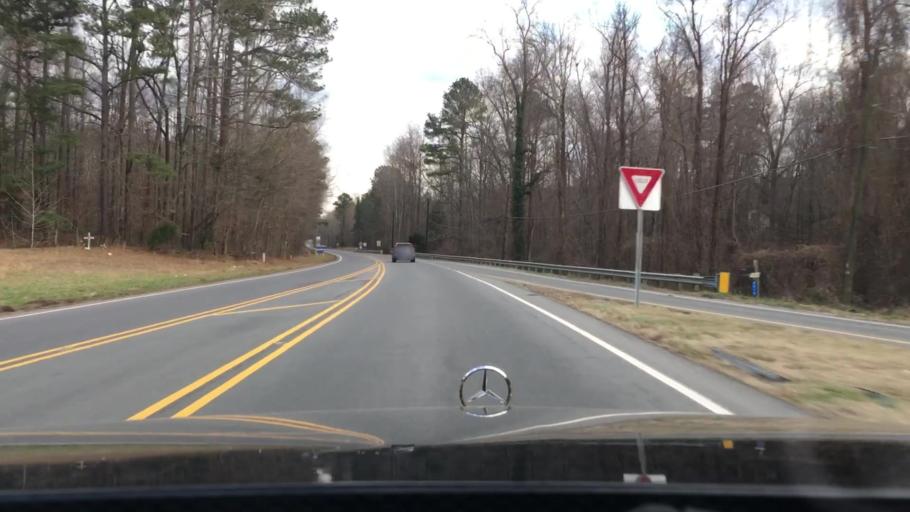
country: US
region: North Carolina
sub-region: Orange County
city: Hillsborough
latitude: 36.0559
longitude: -79.0489
